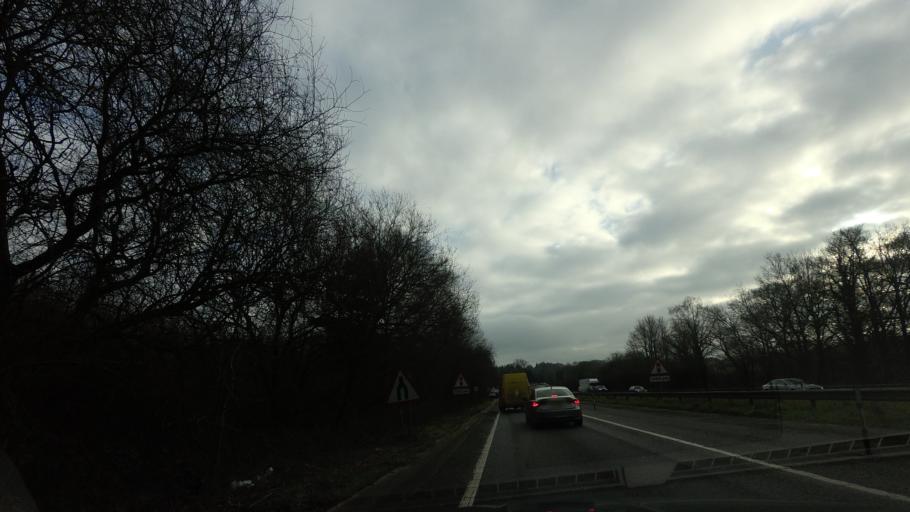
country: GB
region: England
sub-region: Kent
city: Hawkhurst
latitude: 51.0613
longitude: 0.4443
